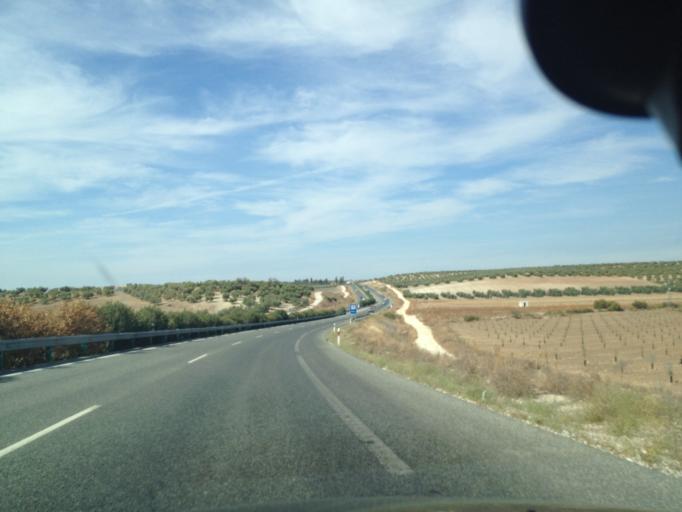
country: ES
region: Andalusia
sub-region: Provincia de Sevilla
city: La Puebla de Cazalla
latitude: 37.2314
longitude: -5.2407
